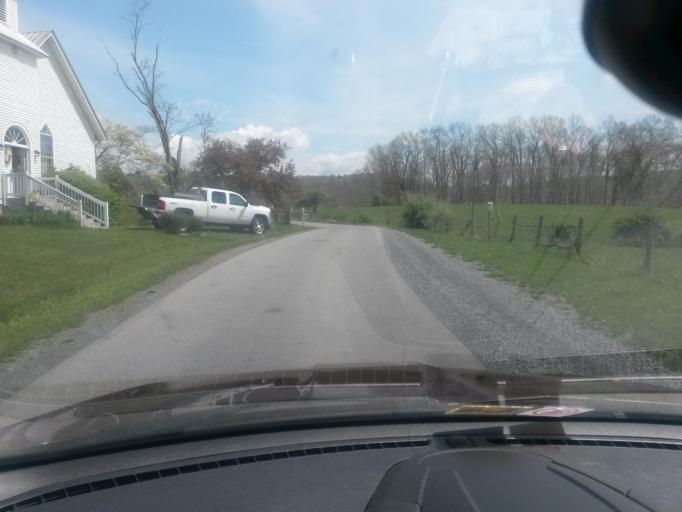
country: US
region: West Virginia
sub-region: Pocahontas County
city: Marlinton
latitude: 38.0805
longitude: -80.2292
